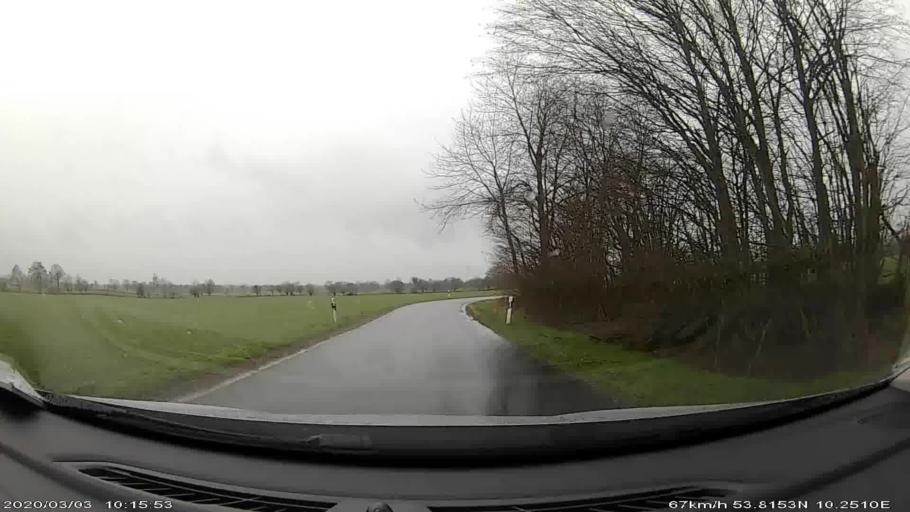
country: DE
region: Schleswig-Holstein
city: Sulfeld
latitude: 53.8134
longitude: 10.2467
